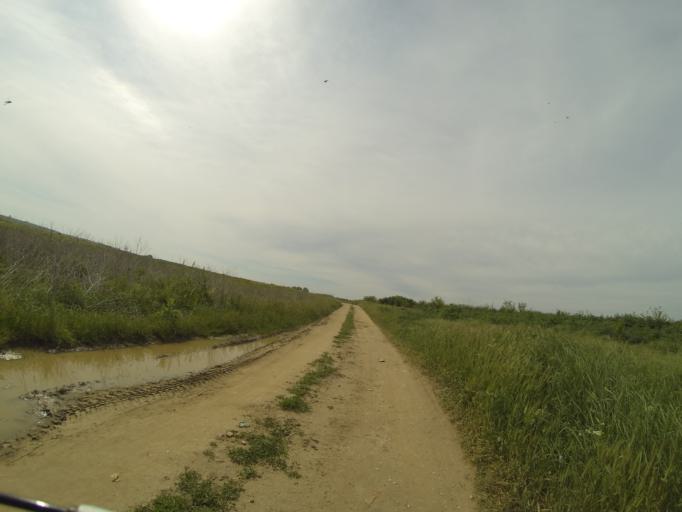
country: RO
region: Dolj
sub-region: Comuna Malu Mare
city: Preajba
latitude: 44.2672
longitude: 23.8632
